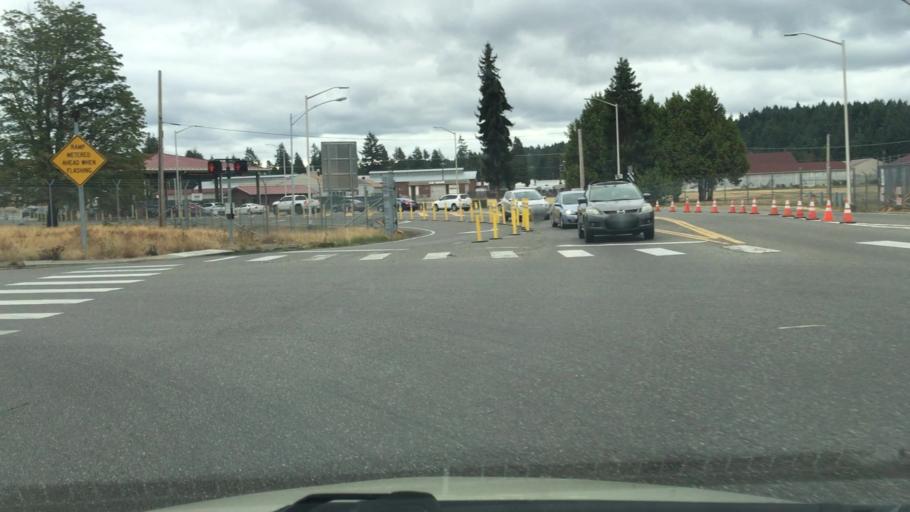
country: US
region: Washington
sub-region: Pierce County
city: DuPont
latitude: 47.0925
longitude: -122.6235
